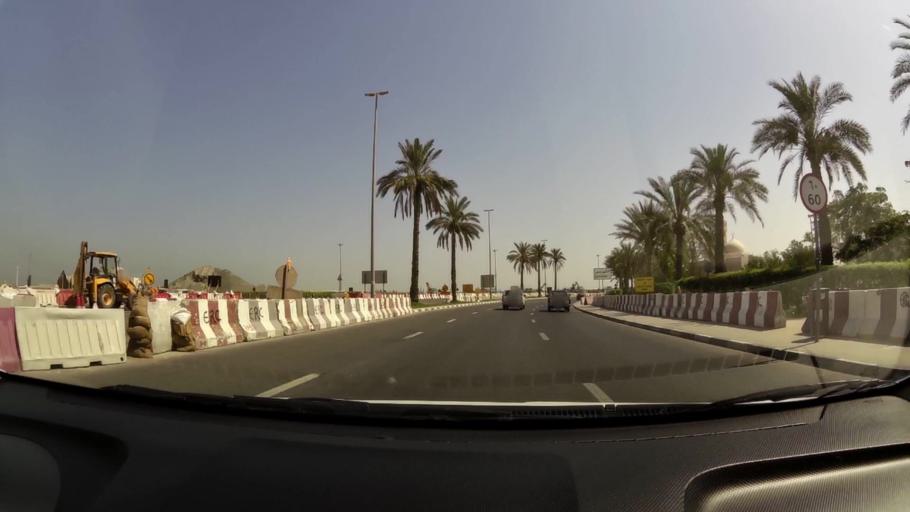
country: AE
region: Ash Shariqah
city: Sharjah
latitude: 25.2747
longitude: 55.2971
